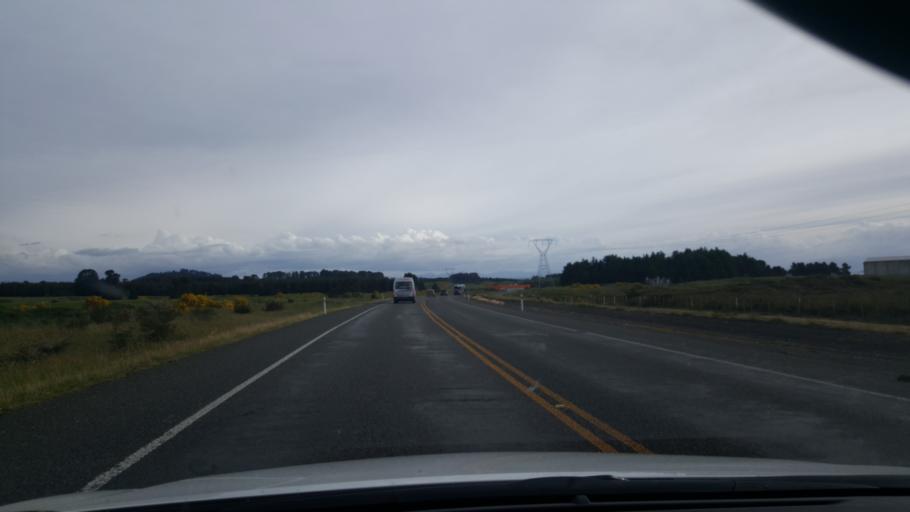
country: NZ
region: Waikato
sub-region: Taupo District
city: Taupo
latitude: -38.6935
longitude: 176.1138
